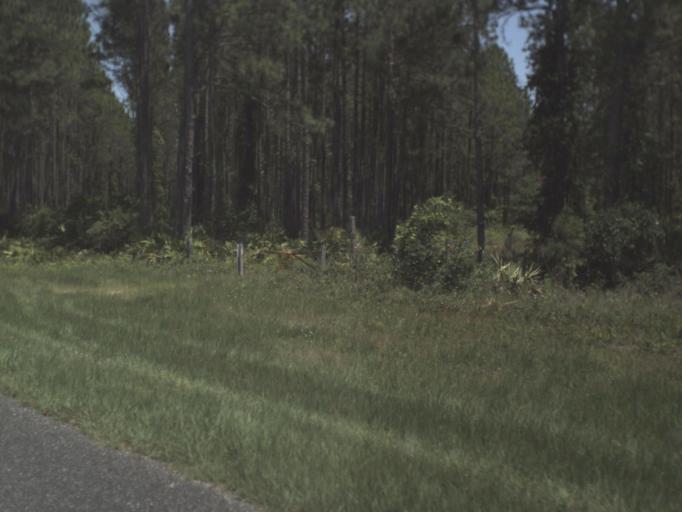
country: US
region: Florida
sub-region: Union County
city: Lake Butler
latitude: 30.2228
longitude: -82.3499
